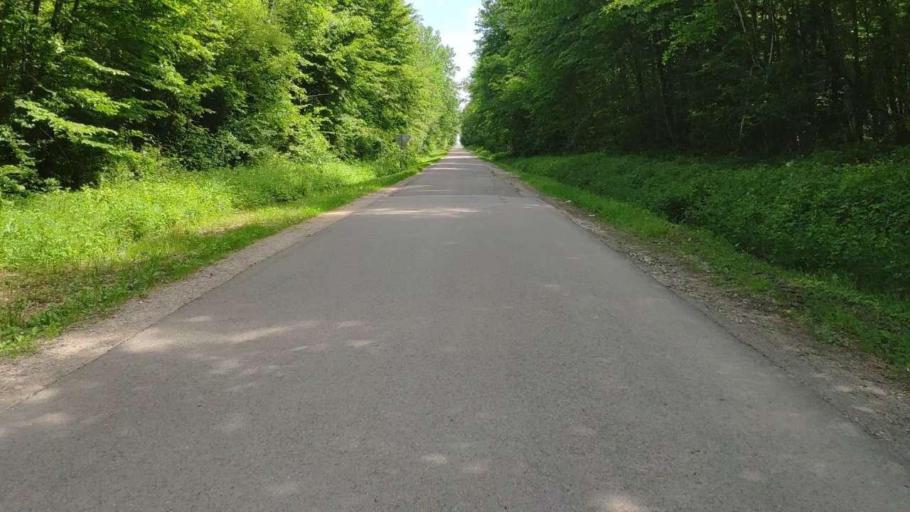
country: FR
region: Franche-Comte
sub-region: Departement du Jura
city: Bletterans
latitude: 46.7106
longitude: 5.4322
